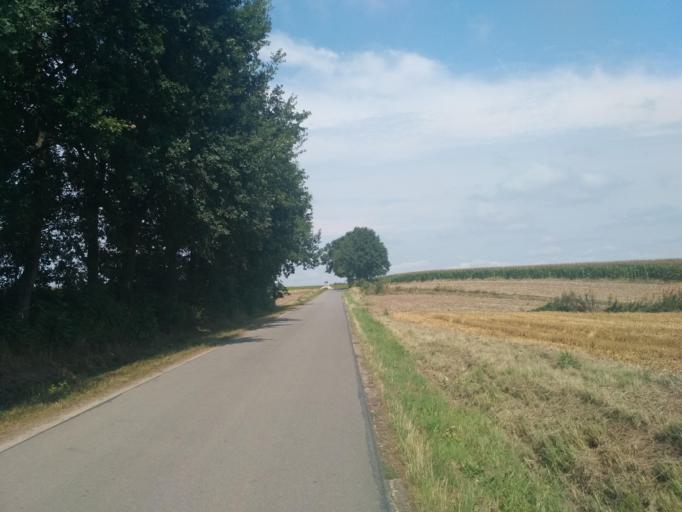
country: PL
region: Subcarpathian Voivodeship
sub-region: Powiat lancucki
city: Krzemienica
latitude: 50.0459
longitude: 22.1960
